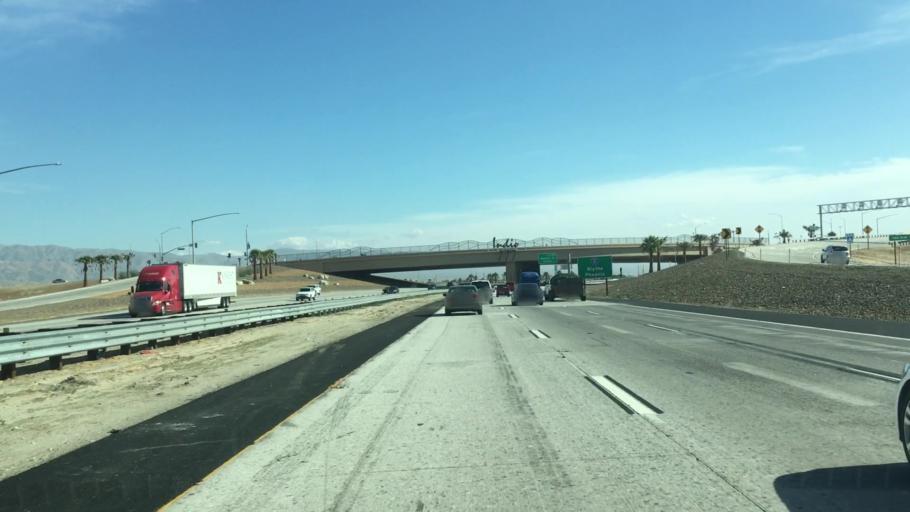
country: US
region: California
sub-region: Riverside County
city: Bermuda Dunes
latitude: 33.7501
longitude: -116.2724
